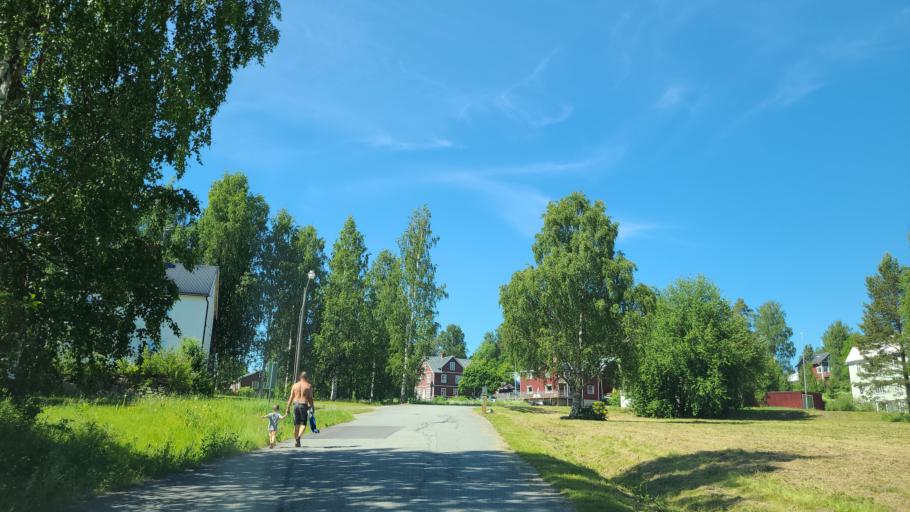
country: SE
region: Vaesterbotten
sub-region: Bjurholms Kommun
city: Bjurholm
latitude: 63.6914
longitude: 18.8642
